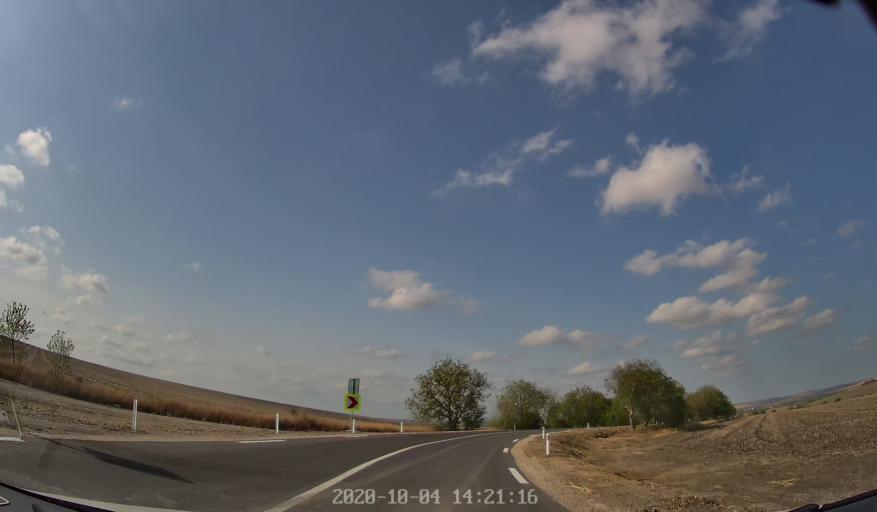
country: MD
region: Rezina
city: Saharna
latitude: 47.5832
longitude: 28.9565
